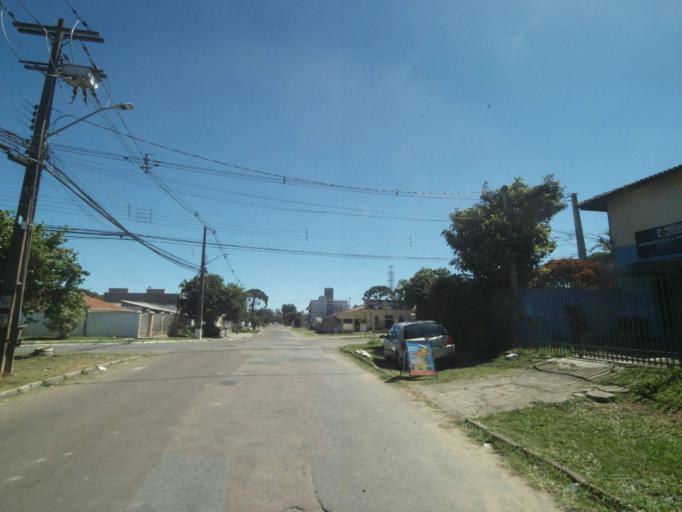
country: BR
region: Parana
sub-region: Curitiba
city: Curitiba
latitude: -25.4810
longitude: -49.3440
